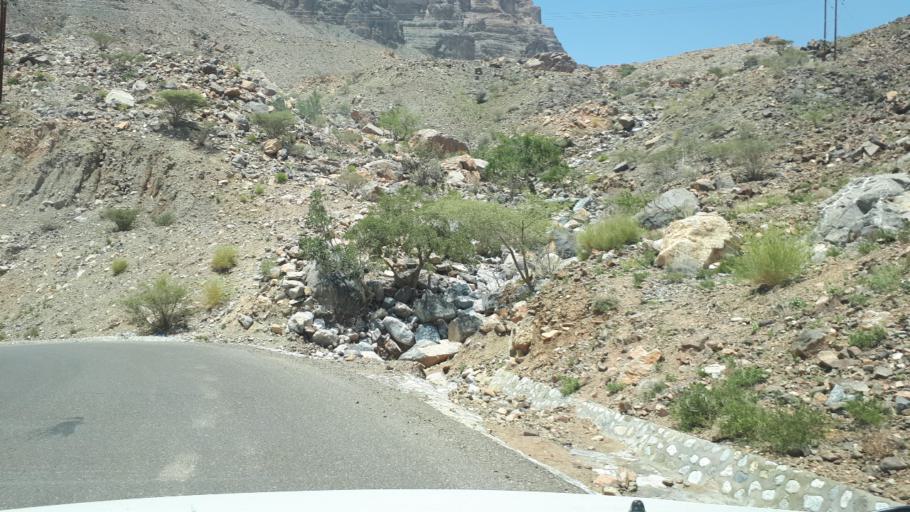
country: OM
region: Muhafazat ad Dakhiliyah
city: Bahla'
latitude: 23.2045
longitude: 57.1448
